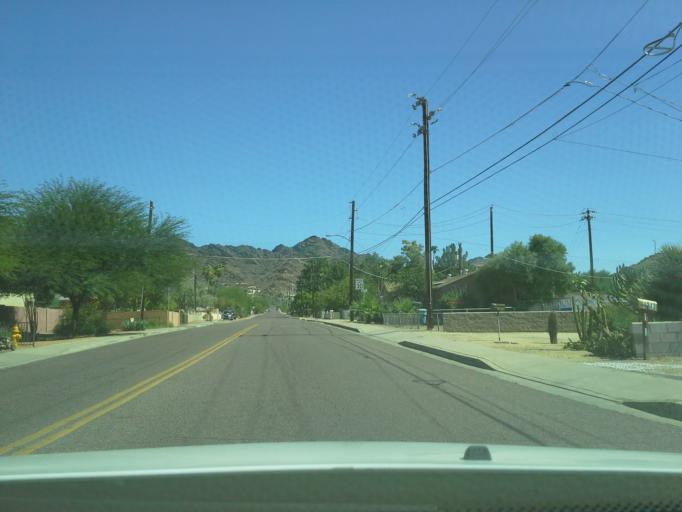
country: US
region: Arizona
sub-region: Maricopa County
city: Paradise Valley
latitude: 33.5749
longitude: -112.0563
